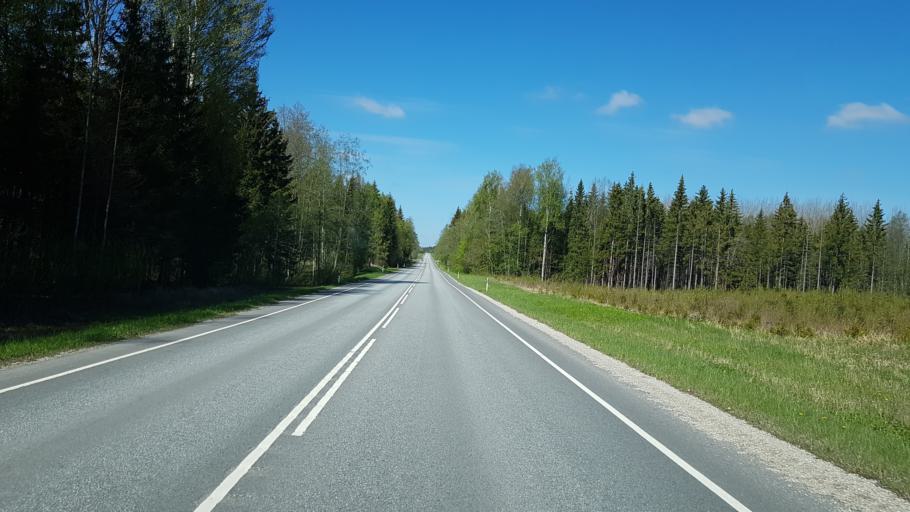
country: EE
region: Valgamaa
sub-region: Torva linn
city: Torva
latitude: 58.0095
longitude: 25.7459
